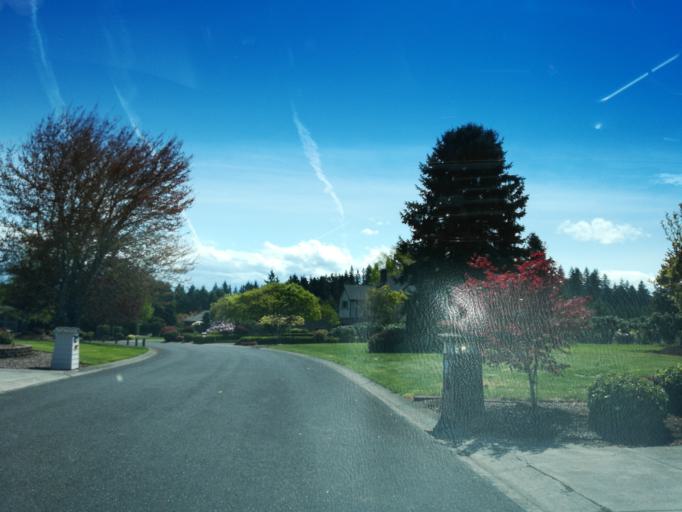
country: US
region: Oregon
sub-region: Clackamas County
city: Damascus
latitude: 45.4286
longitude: -122.4384
